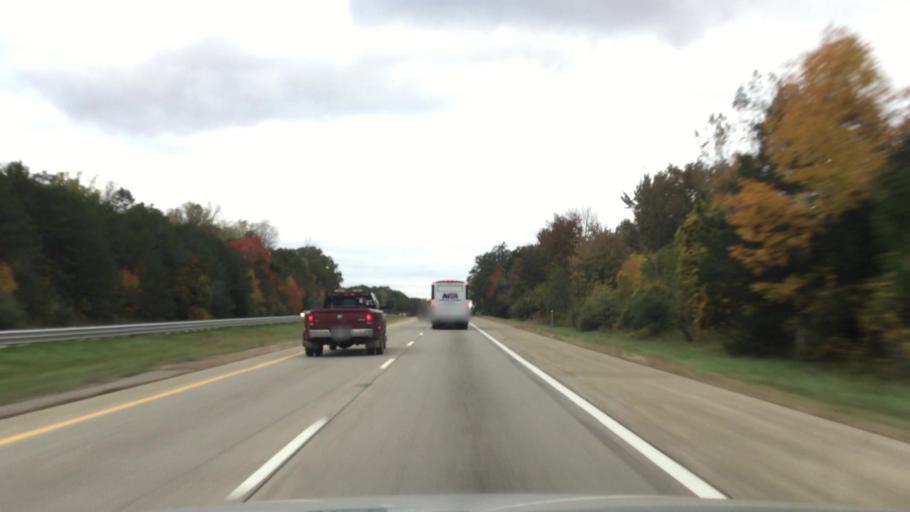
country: US
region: Michigan
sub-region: Genesee County
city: Lake Fenton
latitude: 42.8418
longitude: -83.7366
